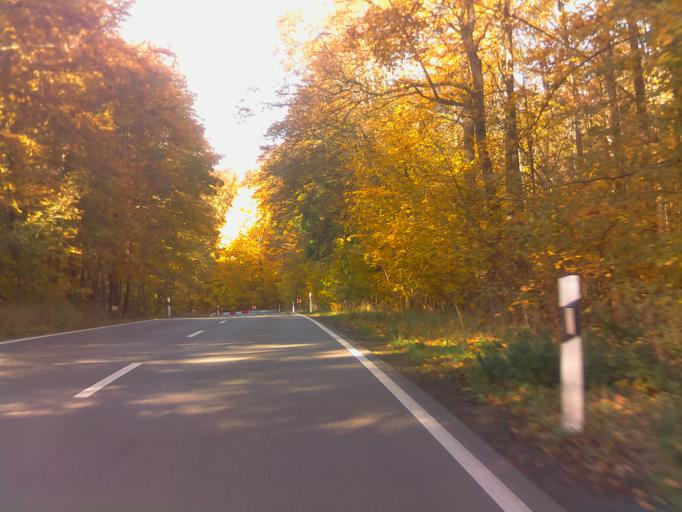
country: DE
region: Bavaria
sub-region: Regierungsbezirk Unterfranken
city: Knetzgau
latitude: 49.9276
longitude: 10.5651
